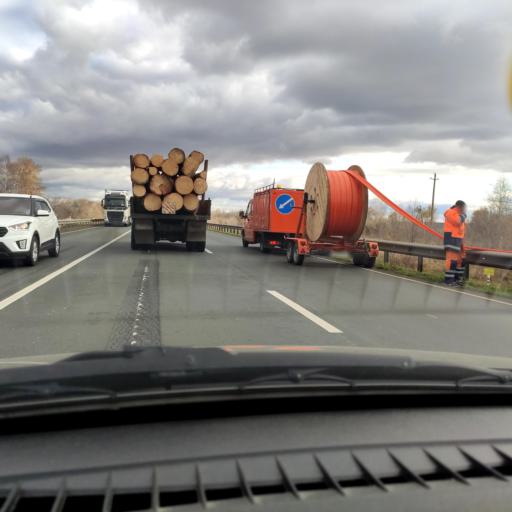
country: RU
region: Samara
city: Syzran'
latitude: 53.2112
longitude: 48.5394
